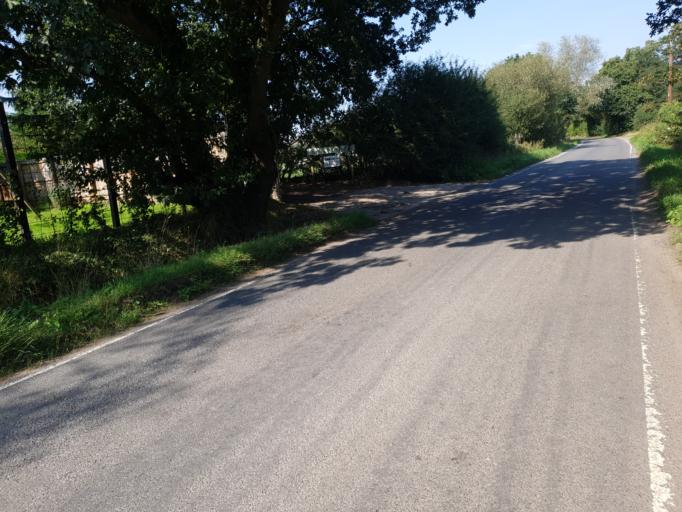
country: GB
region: England
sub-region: Suffolk
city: East Bergholt
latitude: 51.9350
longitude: 0.9931
